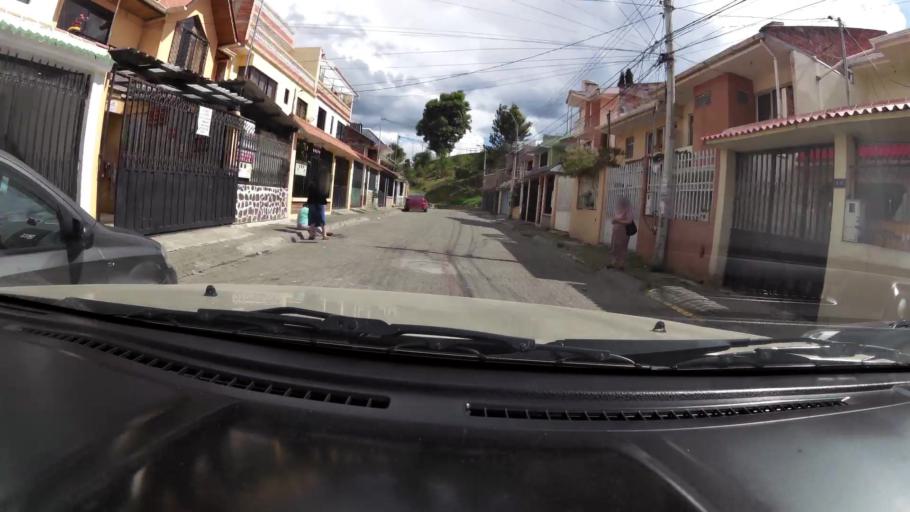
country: EC
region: Azuay
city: Cuenca
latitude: -2.8822
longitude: -78.9826
